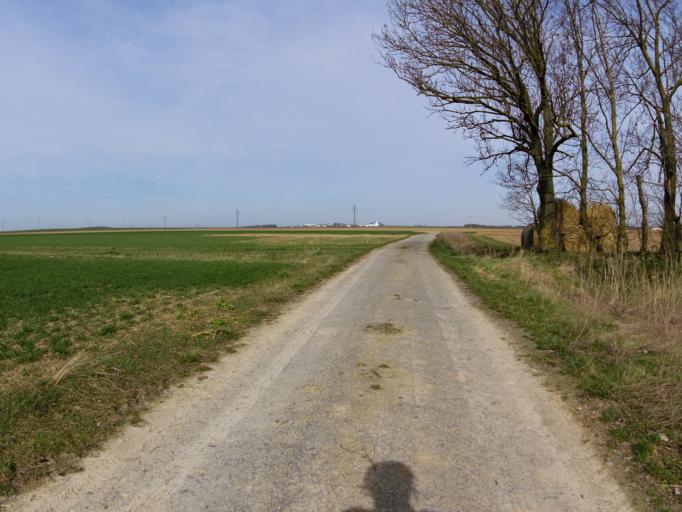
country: DE
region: Bavaria
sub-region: Regierungsbezirk Unterfranken
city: Biebelried
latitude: 49.7506
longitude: 10.0769
